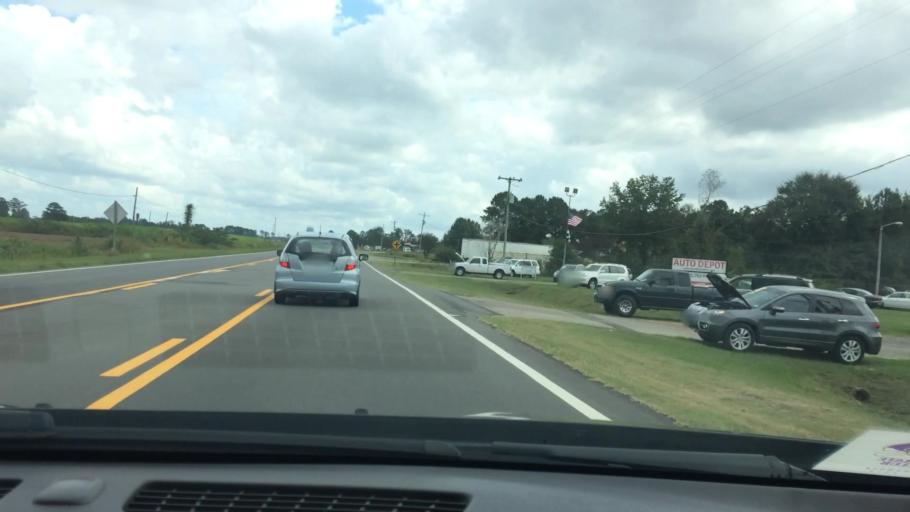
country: US
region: North Carolina
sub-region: Pitt County
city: Farmville
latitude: 35.6062
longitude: -77.6540
